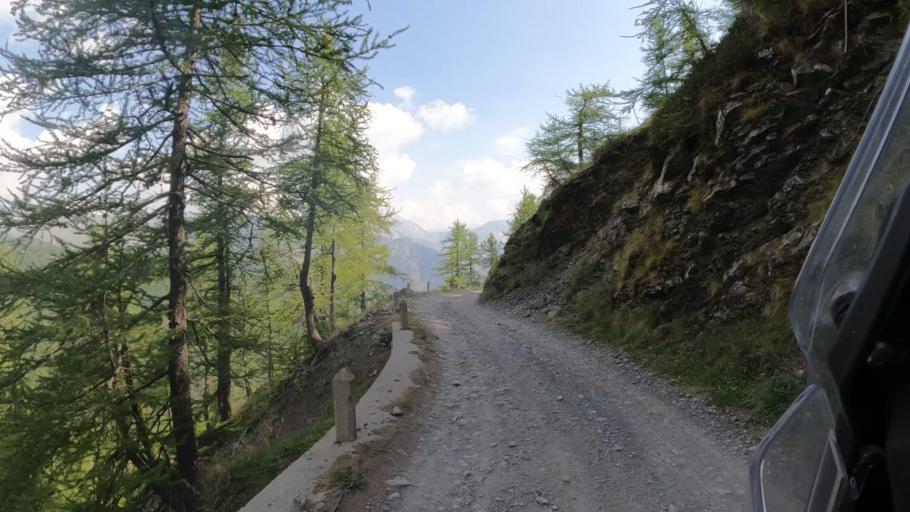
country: IT
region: Piedmont
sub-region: Provincia di Cuneo
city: Briga Alta
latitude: 44.1025
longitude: 7.7170
